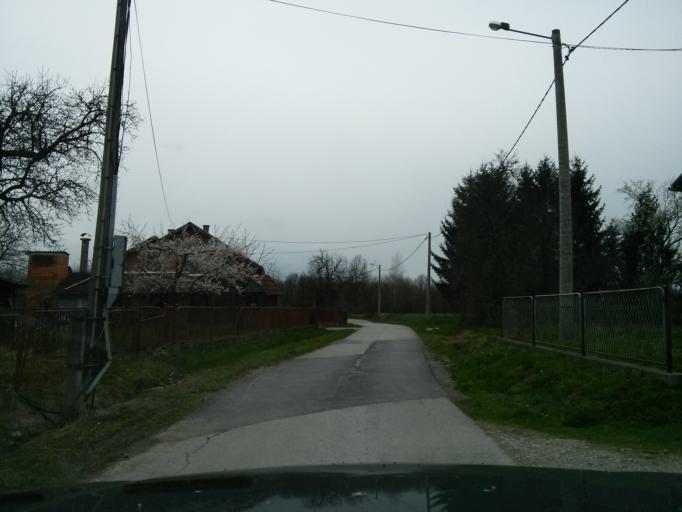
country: HR
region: Sisacko-Moslavacka
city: Gvozd
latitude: 45.2906
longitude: 15.9541
